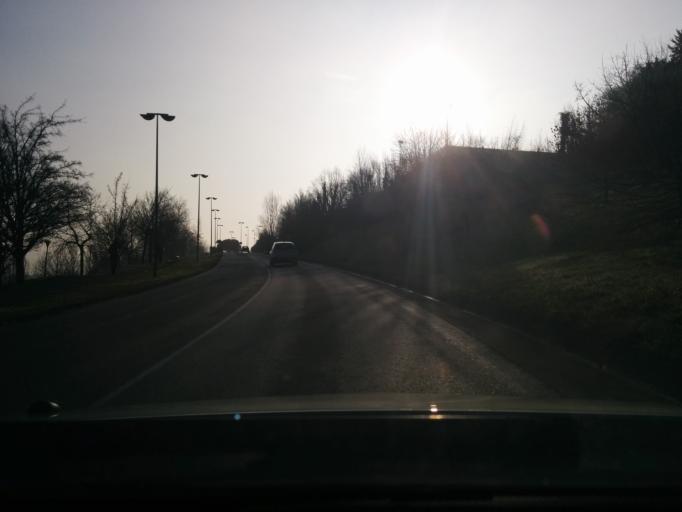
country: ES
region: Navarre
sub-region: Provincia de Navarra
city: Burlata
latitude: 42.8120
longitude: -1.6219
